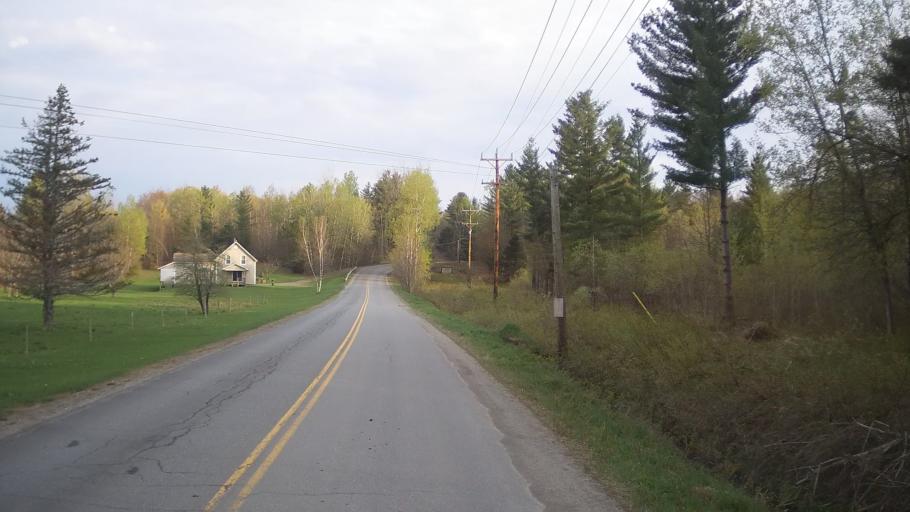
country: US
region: Vermont
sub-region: Orleans County
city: Newport
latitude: 44.9453
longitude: -72.4381
